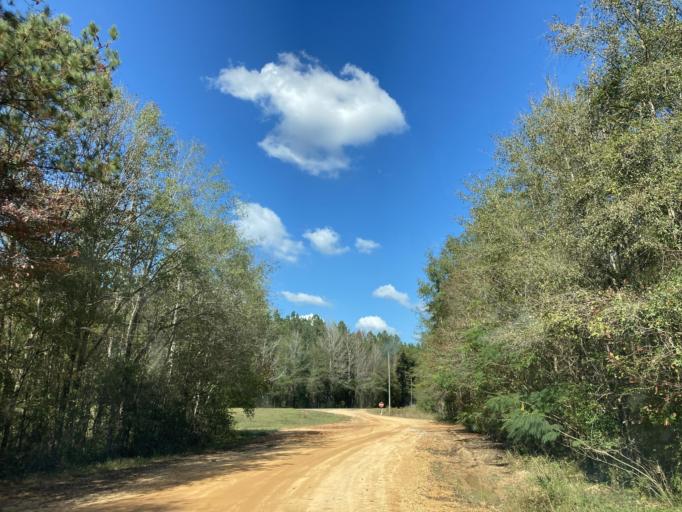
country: US
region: Mississippi
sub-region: Lamar County
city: Sumrall
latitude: 31.3127
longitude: -89.5419
